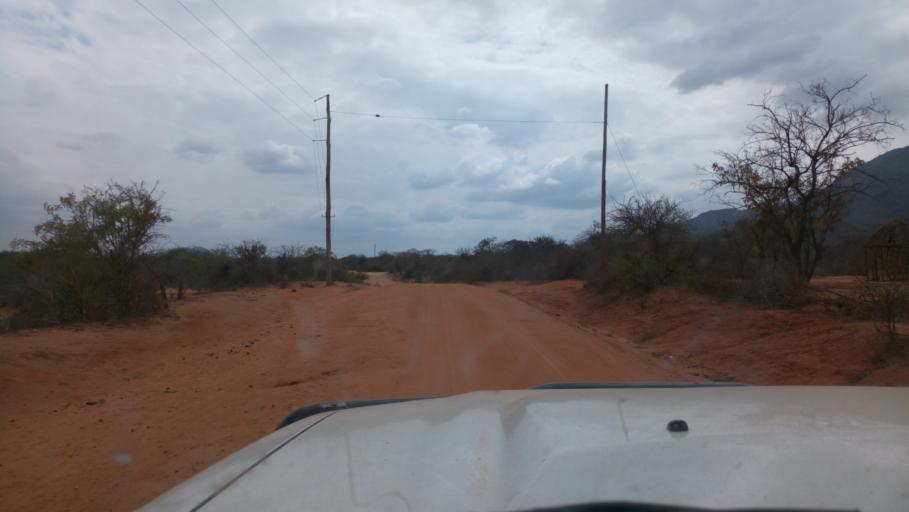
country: KE
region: Kitui
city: Kitui
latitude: -1.8056
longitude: 38.4156
